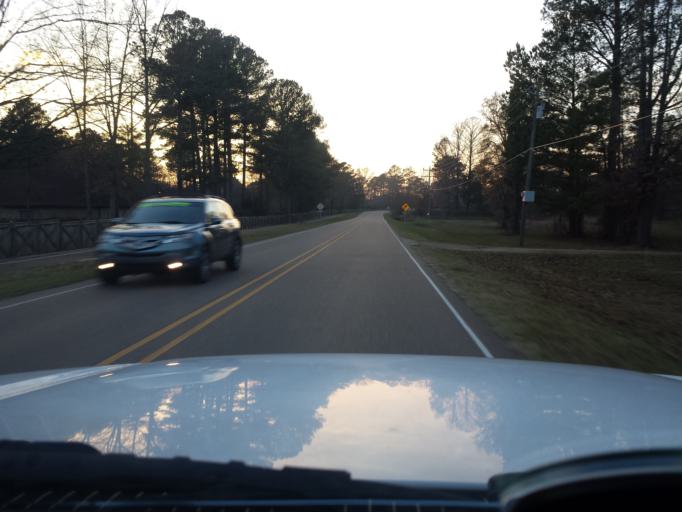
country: US
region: Mississippi
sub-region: Madison County
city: Madison
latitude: 32.4136
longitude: -90.0161
